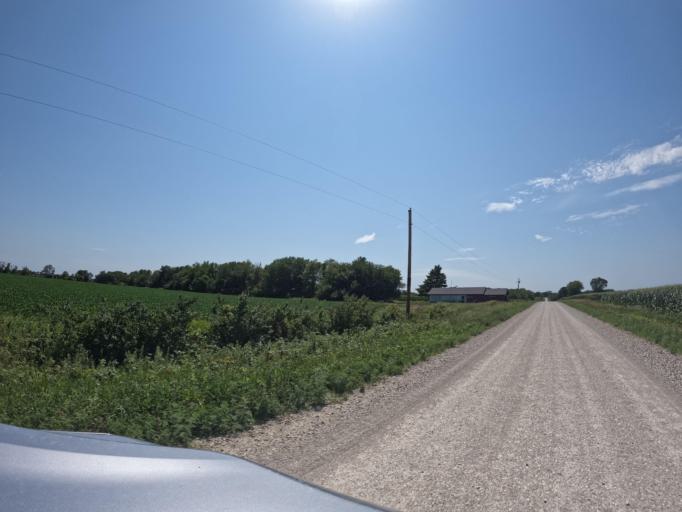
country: US
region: Iowa
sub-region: Henry County
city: Mount Pleasant
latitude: 40.8900
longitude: -91.6455
